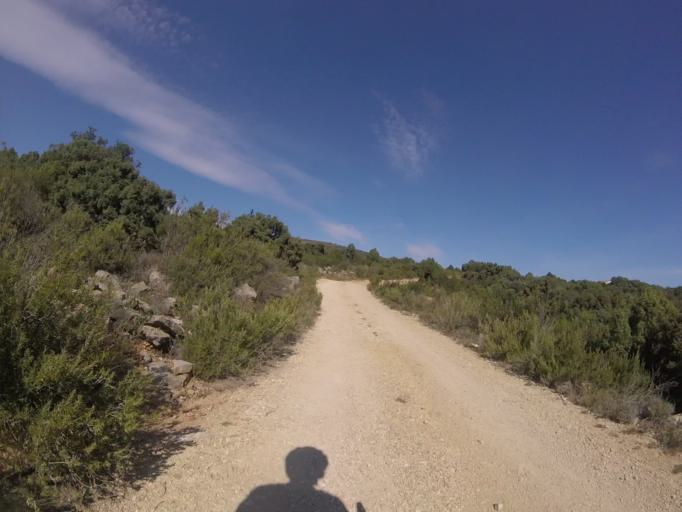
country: ES
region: Valencia
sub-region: Provincia de Castello
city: Sierra-Engarceran
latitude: 40.2705
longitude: 0.0153
